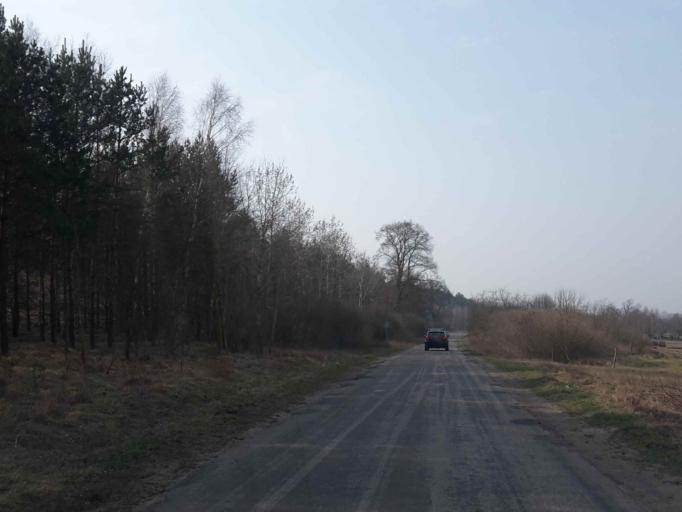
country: PL
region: Kujawsko-Pomorskie
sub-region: Powiat nakielski
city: Sadki
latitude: 53.0862
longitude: 17.4743
